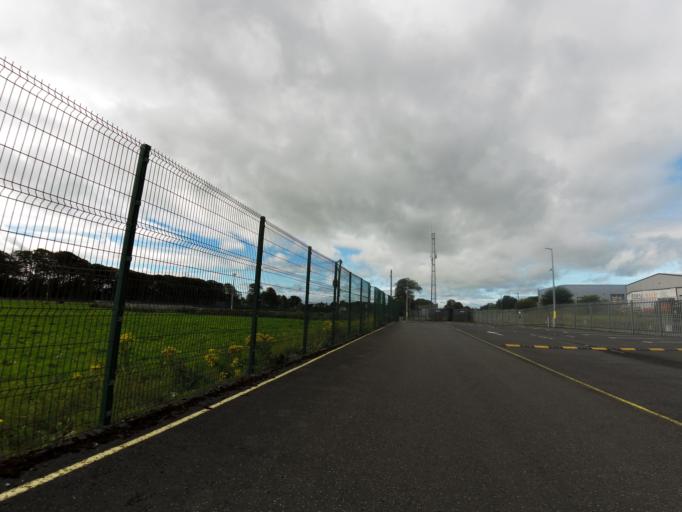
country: IE
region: Connaught
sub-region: County Galway
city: Athenry
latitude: 53.2998
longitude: -8.7512
